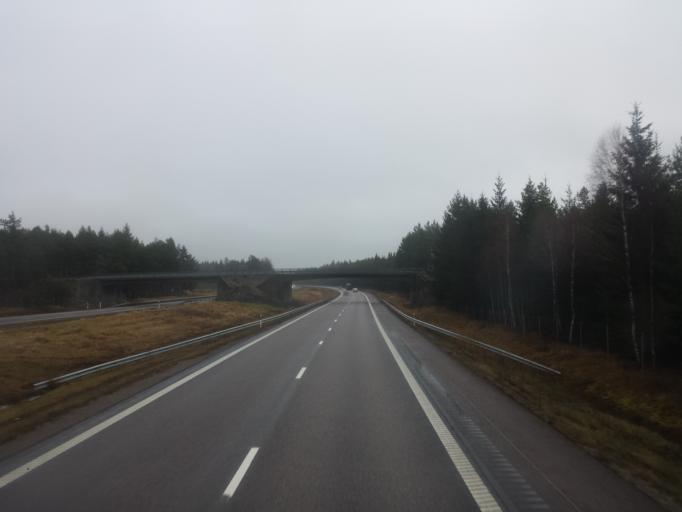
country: SE
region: Soedermanland
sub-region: Nykopings Kommun
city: Stigtomta
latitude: 58.7577
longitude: 16.8130
